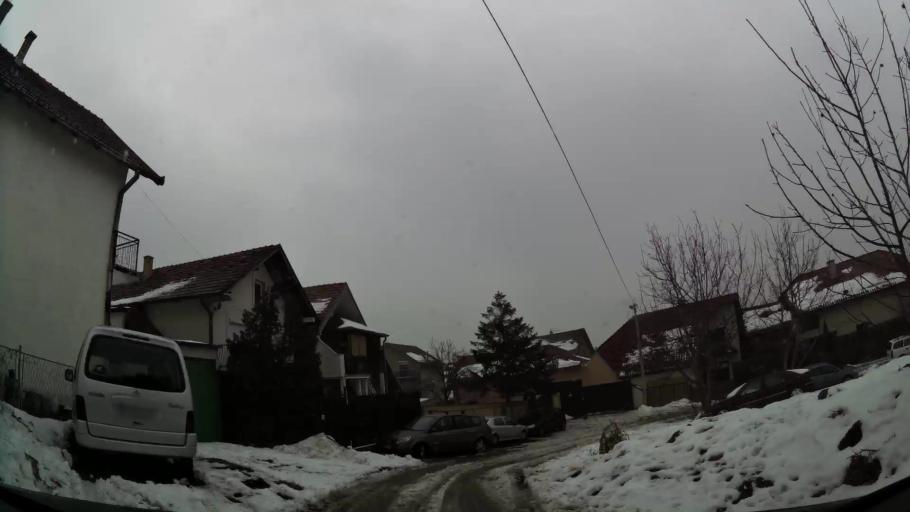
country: RS
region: Central Serbia
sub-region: Belgrade
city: Zvezdara
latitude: 44.7783
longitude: 20.5180
